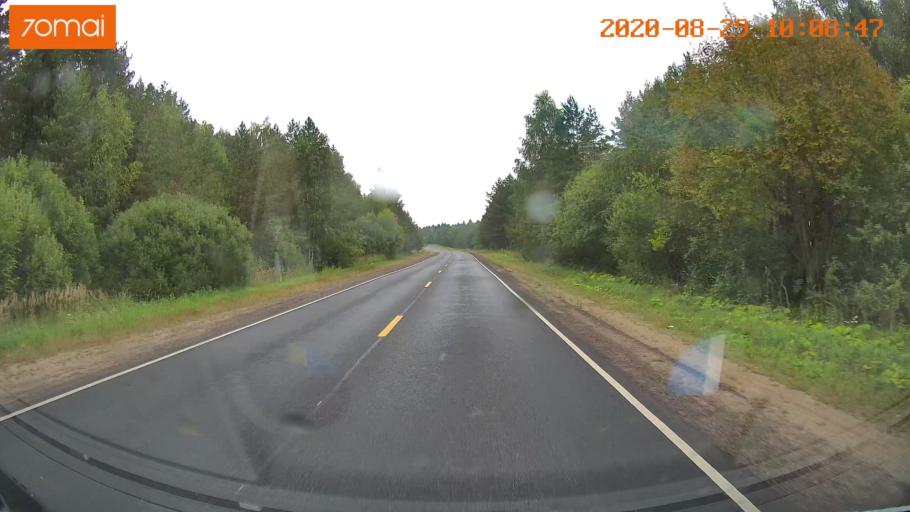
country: RU
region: Ivanovo
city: Kuznechikha
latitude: 57.3748
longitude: 42.5991
